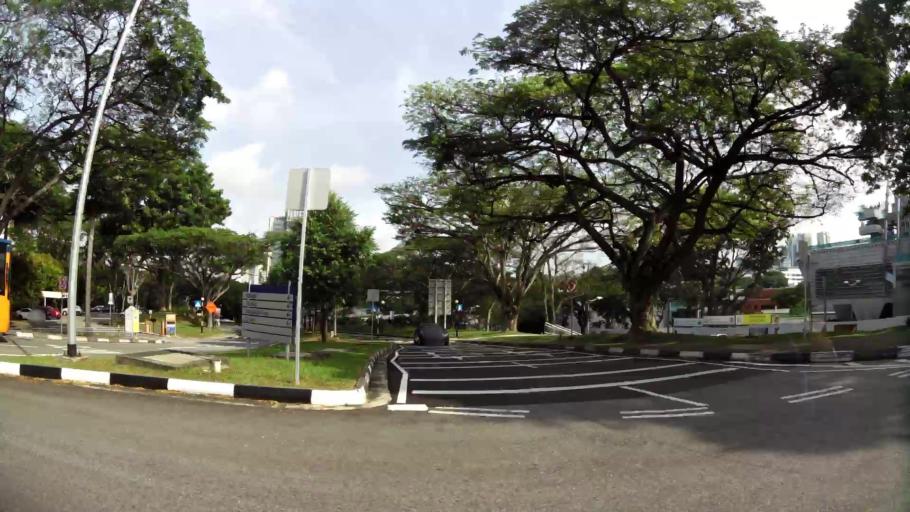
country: SG
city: Singapore
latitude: 1.2997
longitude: 103.7746
